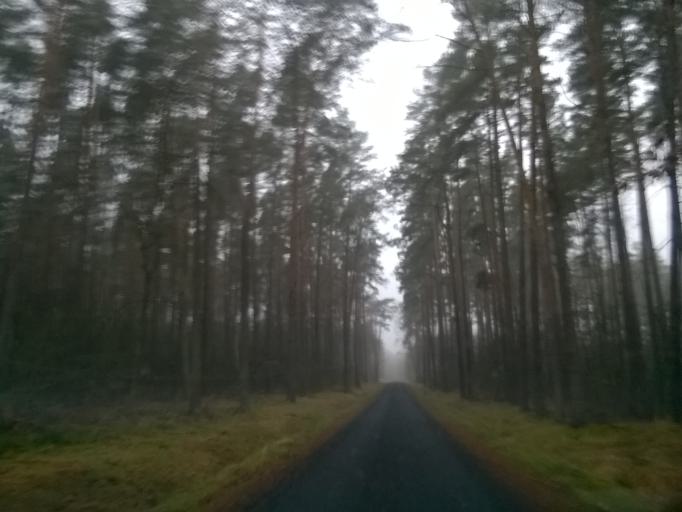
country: PL
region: Kujawsko-Pomorskie
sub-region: Powiat nakielski
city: Kcynia
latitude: 53.0424
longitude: 17.5108
